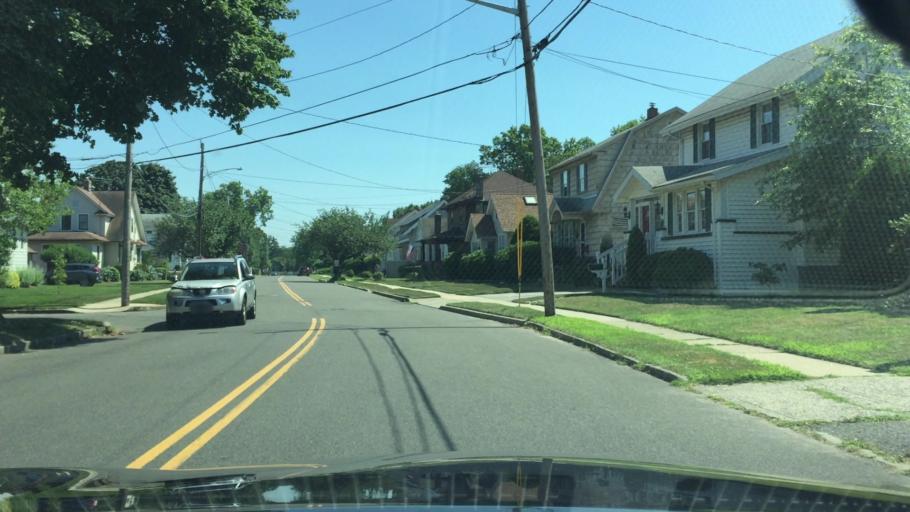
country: US
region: Connecticut
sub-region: Fairfield County
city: Stratford
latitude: 41.1857
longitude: -73.1345
